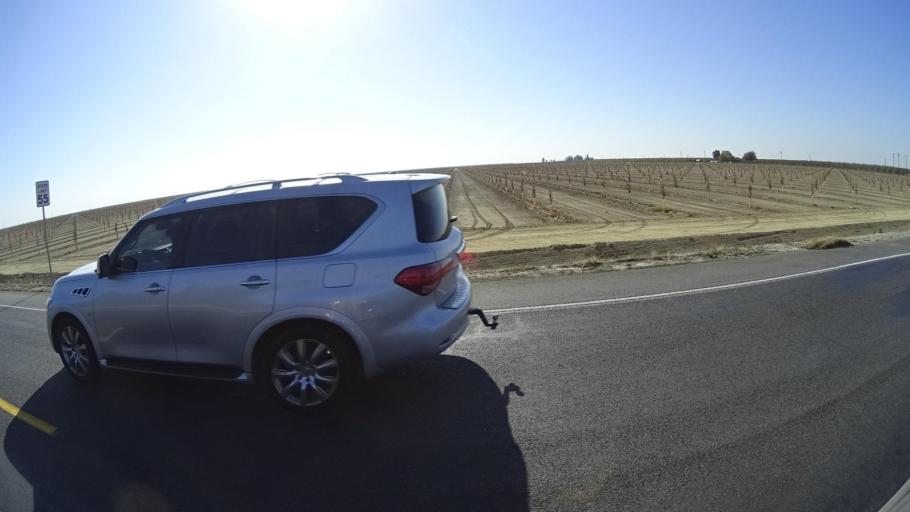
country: US
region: California
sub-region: Kern County
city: Delano
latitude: 35.7179
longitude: -119.3090
